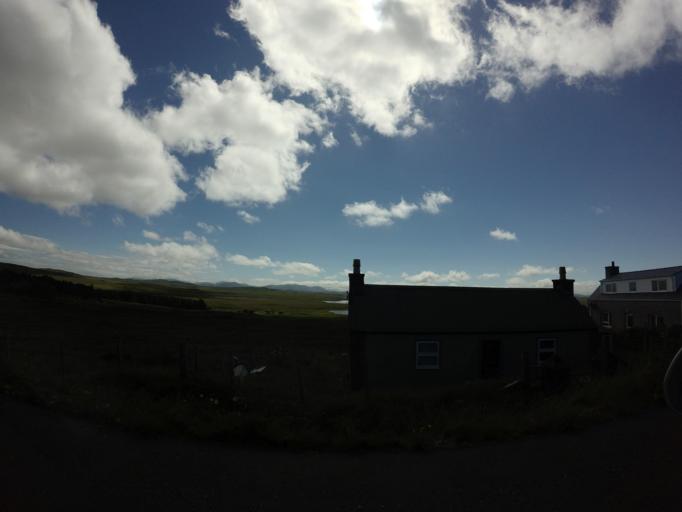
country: GB
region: Scotland
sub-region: Eilean Siar
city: Stornoway
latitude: 58.1682
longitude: -6.5643
